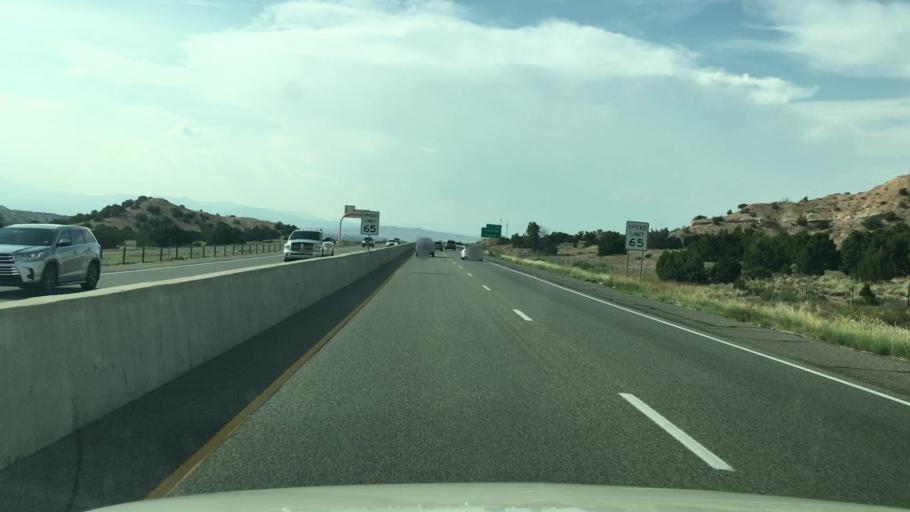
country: US
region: New Mexico
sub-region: Santa Fe County
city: Nambe
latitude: 35.8300
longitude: -105.9814
